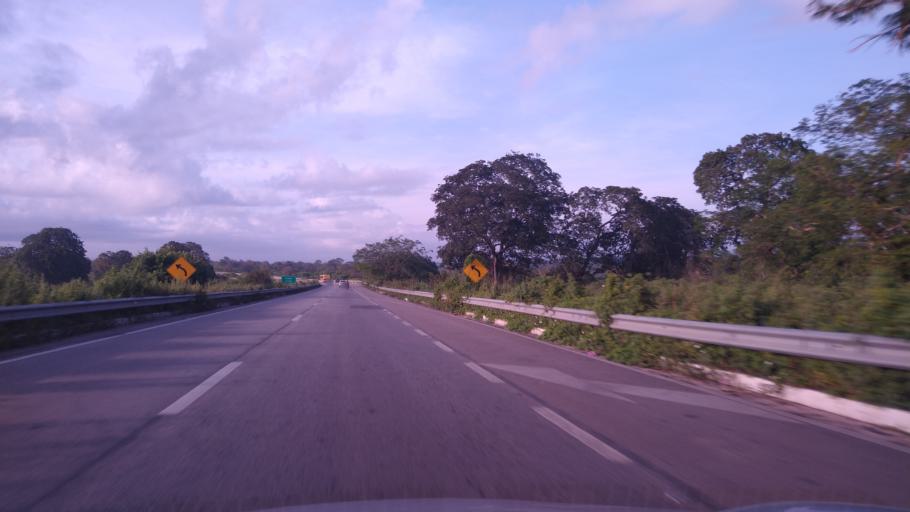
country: BR
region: Ceara
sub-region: Pacajus
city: Pacajus
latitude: -4.1782
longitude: -38.4922
